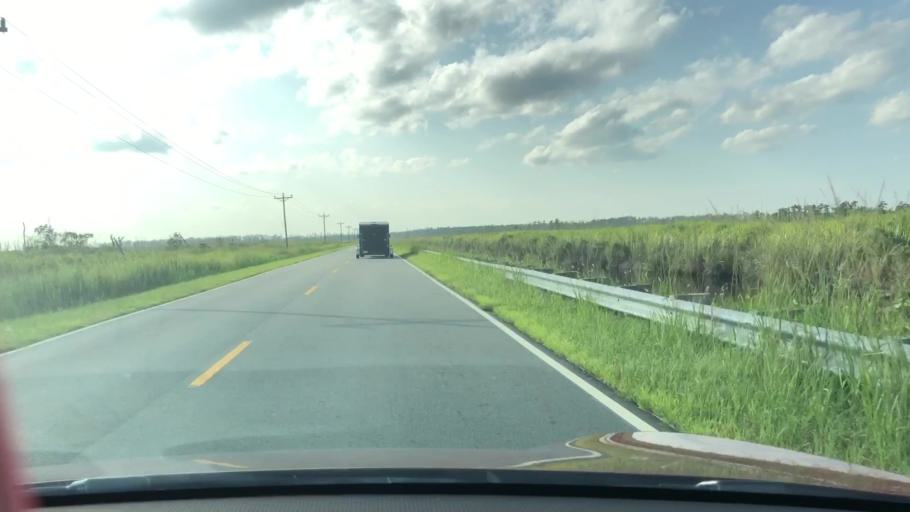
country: US
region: North Carolina
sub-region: Dare County
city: Wanchese
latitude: 35.6283
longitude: -75.8500
